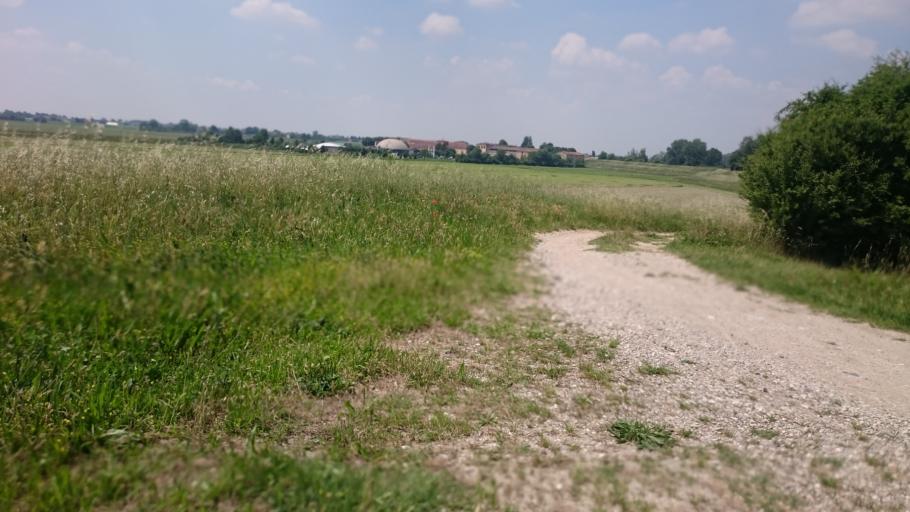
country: IT
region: Lombardy
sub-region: Provincia di Mantova
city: San Biagio
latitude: 45.1260
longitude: 10.8422
